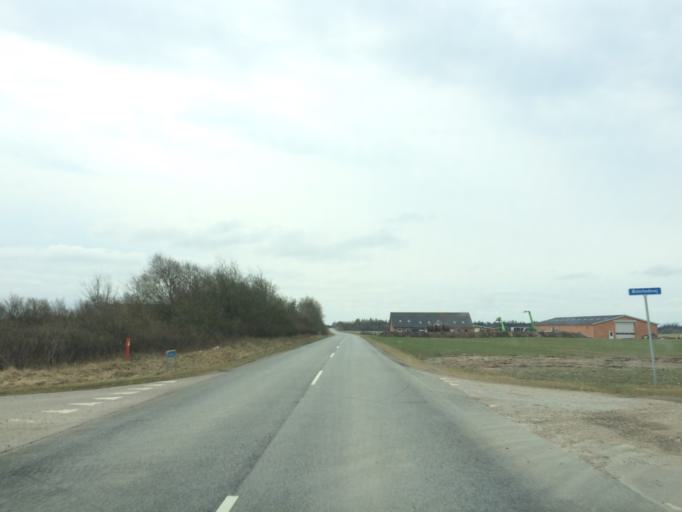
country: DK
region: Central Jutland
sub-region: Ringkobing-Skjern Kommune
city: Tarm
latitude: 55.8418
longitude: 8.4706
